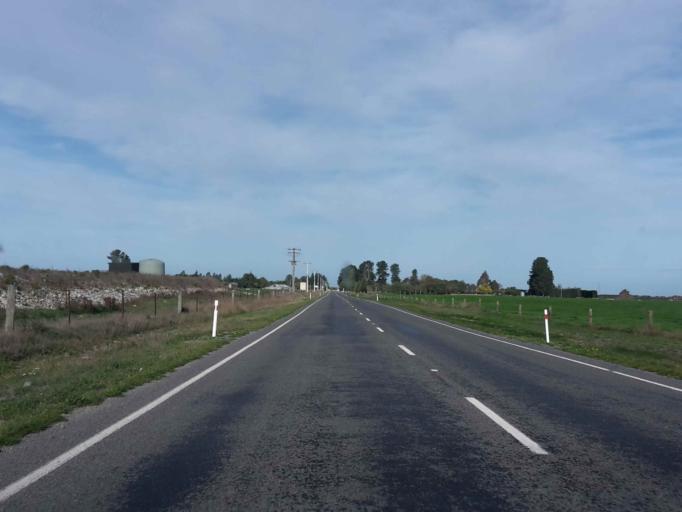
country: NZ
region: Canterbury
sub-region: Timaru District
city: Pleasant Point
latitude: -44.0593
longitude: 171.3518
